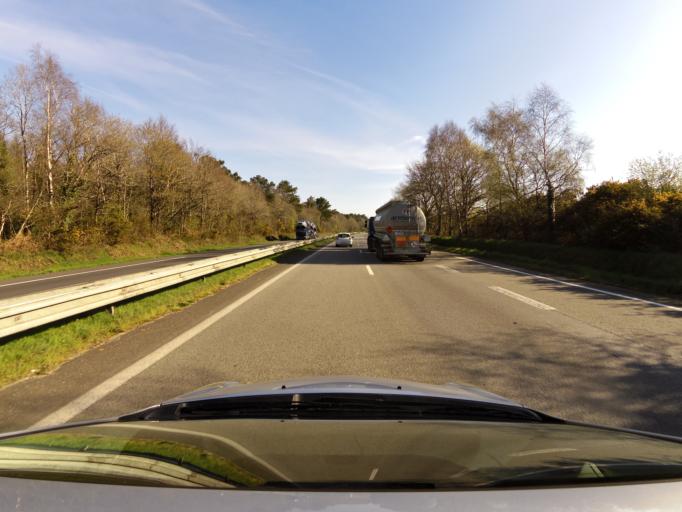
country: FR
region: Brittany
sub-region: Departement du Morbihan
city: Hennebont
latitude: 47.8005
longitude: -3.2384
